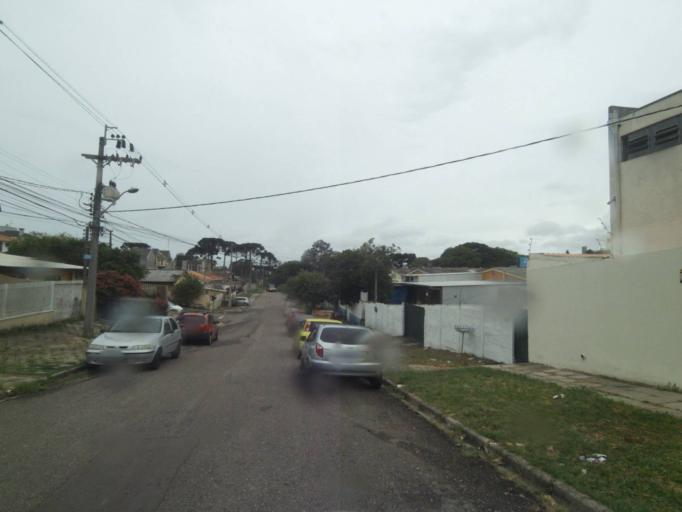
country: BR
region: Parana
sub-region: Curitiba
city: Curitiba
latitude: -25.4297
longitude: -49.3297
